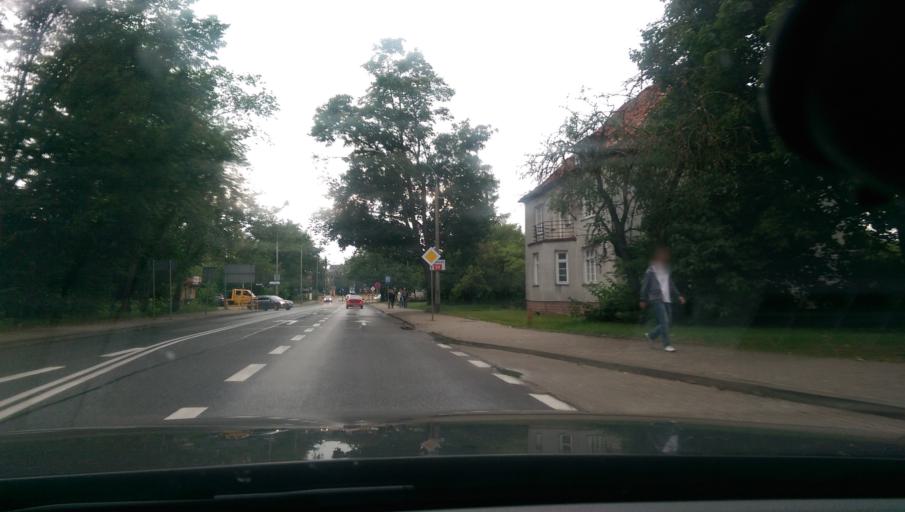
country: PL
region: Warmian-Masurian Voivodeship
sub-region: Powiat szczycienski
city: Szczytno
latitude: 53.5608
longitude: 21.0054
